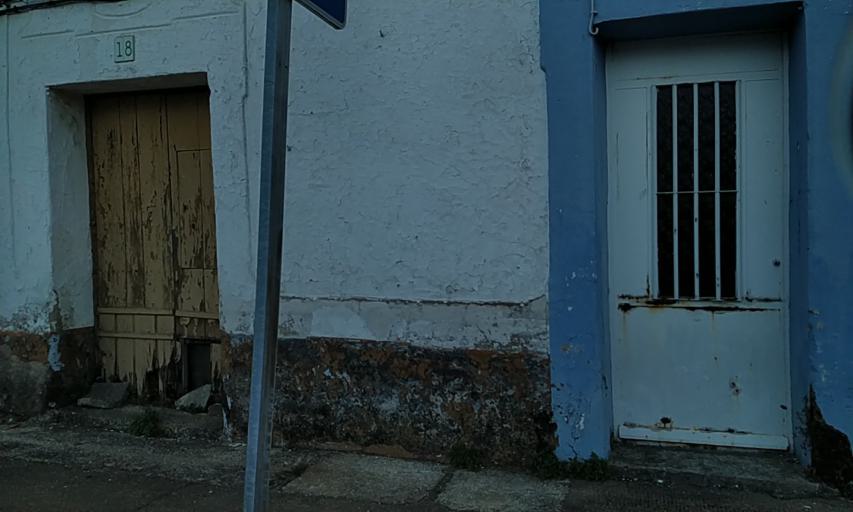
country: PT
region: Portalegre
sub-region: Portalegre
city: Sao Juliao
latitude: 39.3488
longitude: -7.2753
